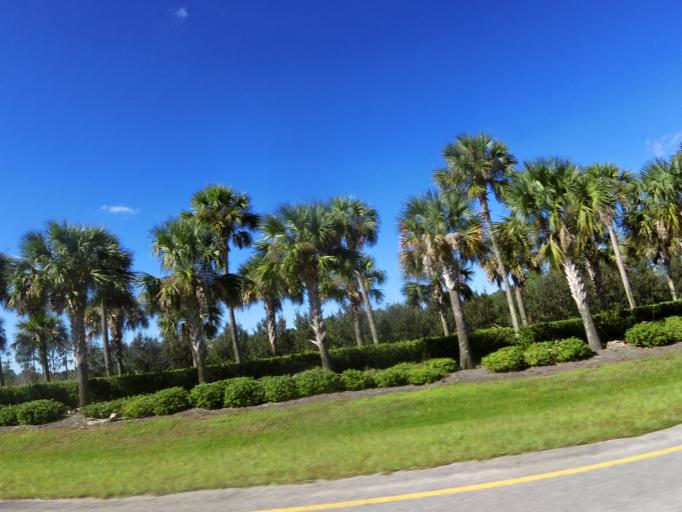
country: US
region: Florida
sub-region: Saint Johns County
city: Palm Valley
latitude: 30.1146
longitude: -81.4154
